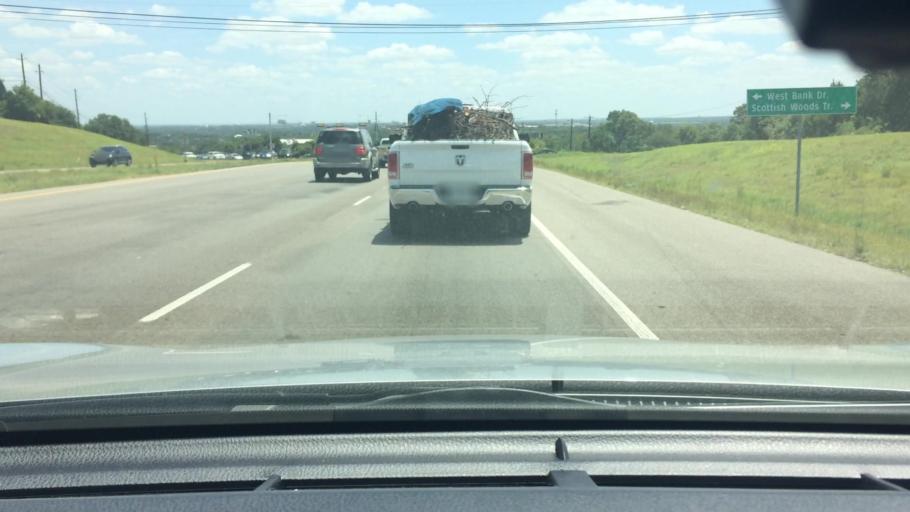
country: US
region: Texas
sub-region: Travis County
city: West Lake Hills
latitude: 30.2788
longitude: -97.8208
